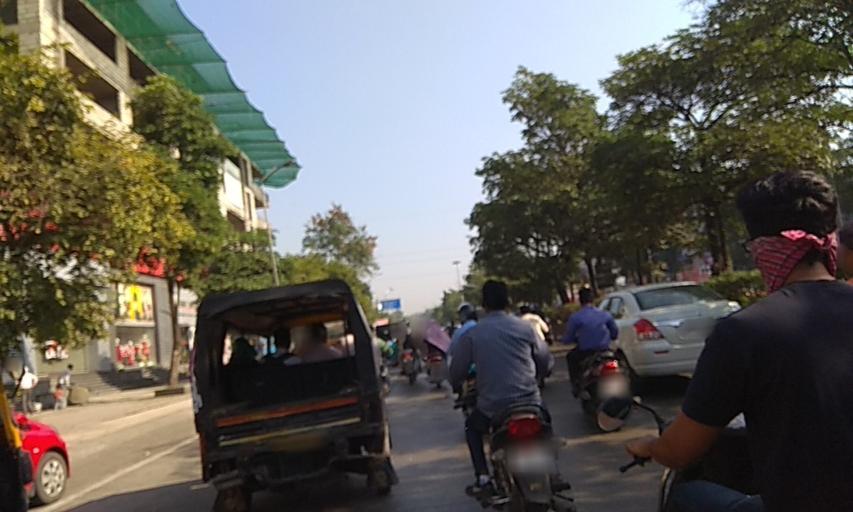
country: IN
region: Maharashtra
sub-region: Pune Division
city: Pune
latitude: 18.4800
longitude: 73.8249
